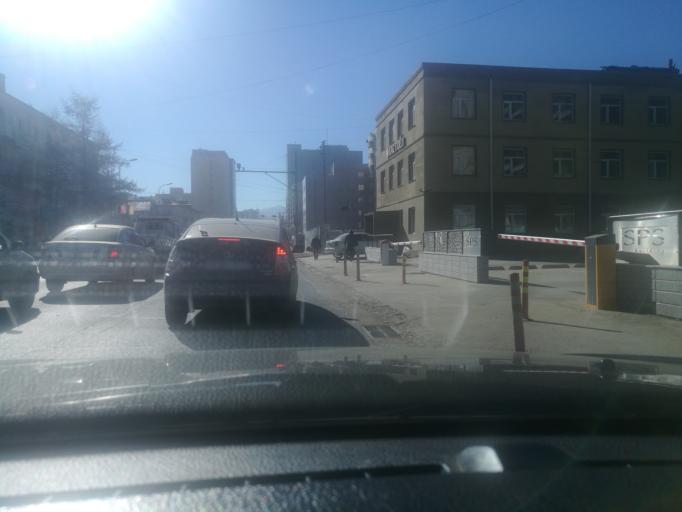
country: MN
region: Ulaanbaatar
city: Ulaanbaatar
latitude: 47.9299
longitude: 106.9169
